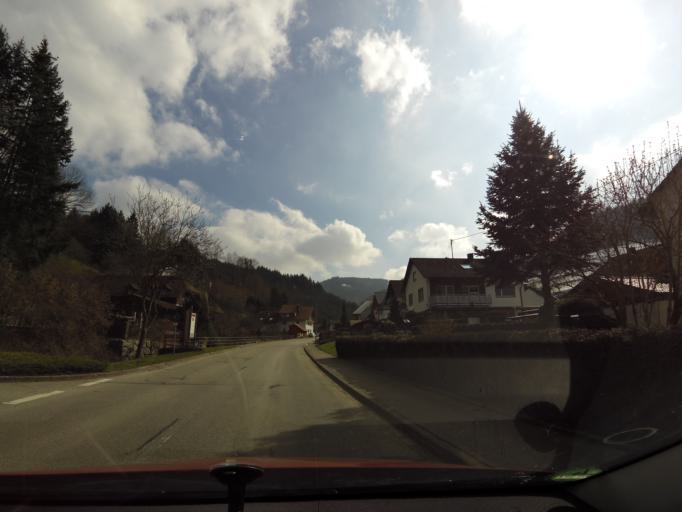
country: DE
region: Baden-Wuerttemberg
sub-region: Freiburg Region
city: Ottenhofen im Schwarzwald
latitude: 48.5566
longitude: 8.1540
